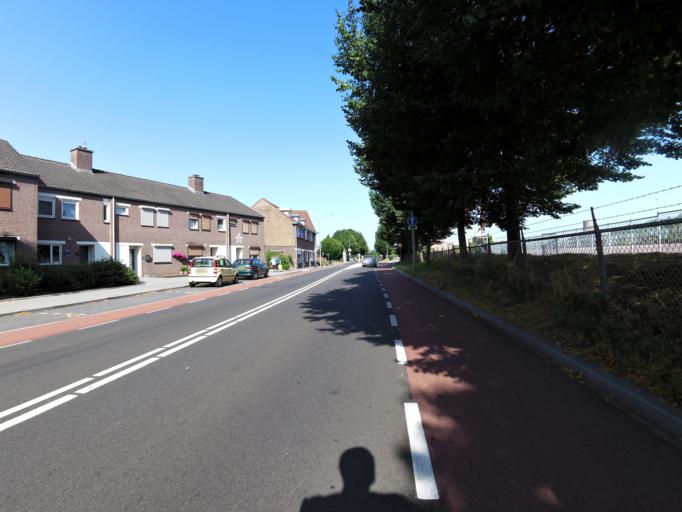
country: NL
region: Limburg
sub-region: Gemeente Heerlen
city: Heerlen
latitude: 50.8919
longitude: 5.9655
